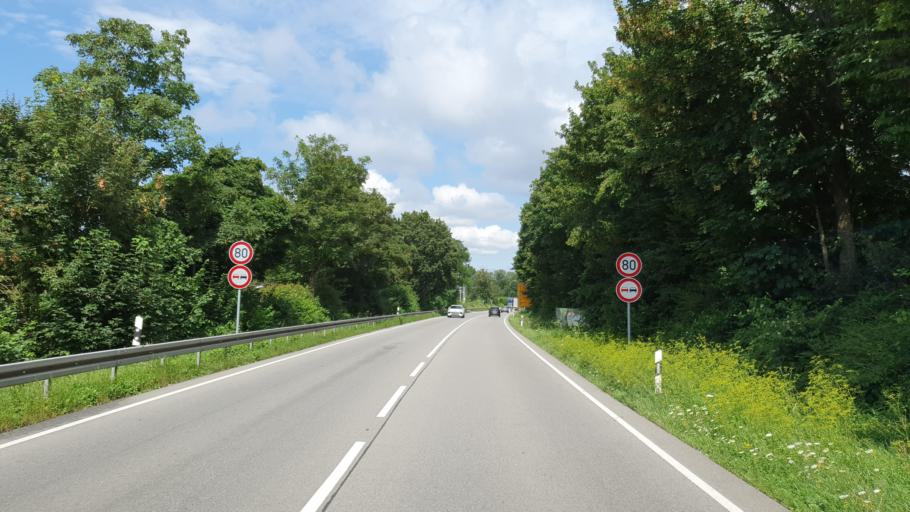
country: DE
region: Baden-Wuerttemberg
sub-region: Tuebingen Region
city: Friedrichshafen
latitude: 47.6537
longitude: 9.5023
